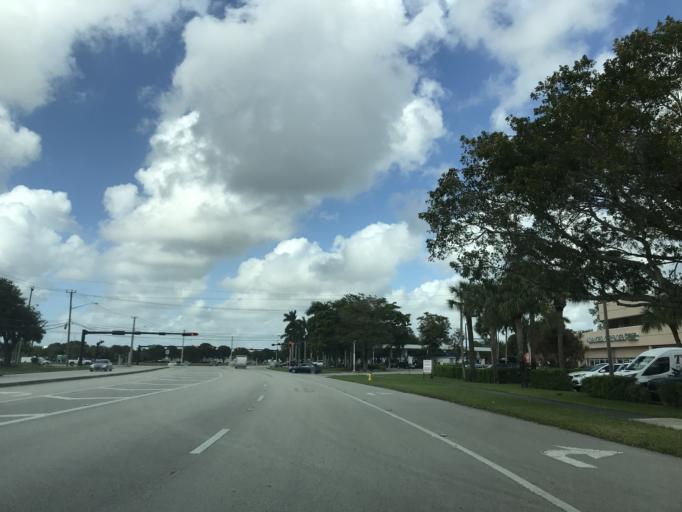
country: US
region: Florida
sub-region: Broward County
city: Margate
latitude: 26.2542
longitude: -80.1946
